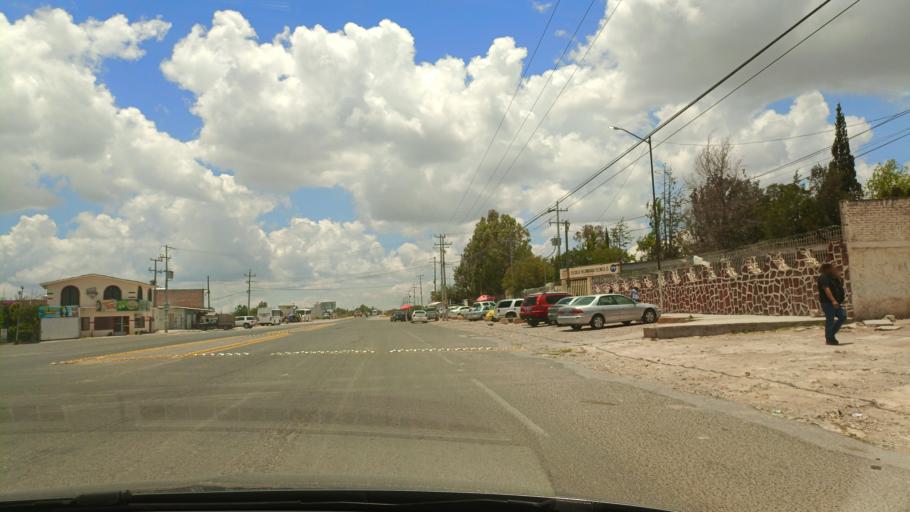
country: MX
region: Guerrero
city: San Luis de la Paz
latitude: 21.2884
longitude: -100.5100
